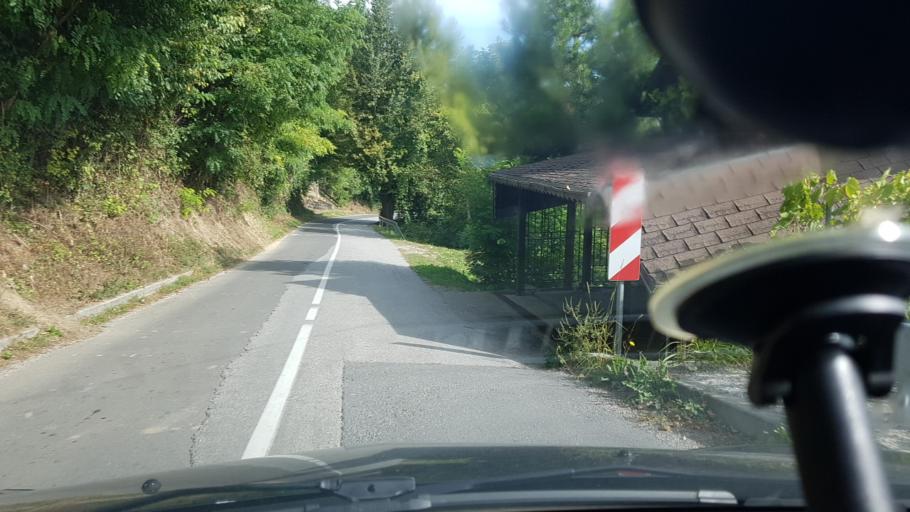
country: HR
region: Varazdinska
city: Remetinec
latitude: 46.1090
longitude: 16.2215
